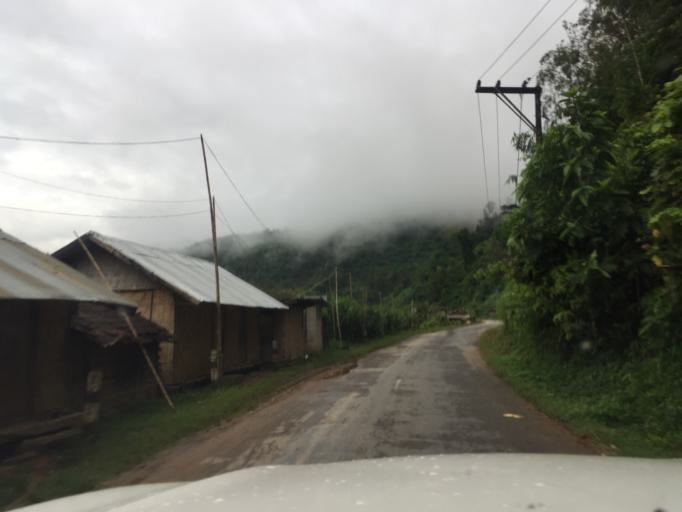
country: LA
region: Oudomxai
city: Muang La
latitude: 20.9087
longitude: 102.1855
